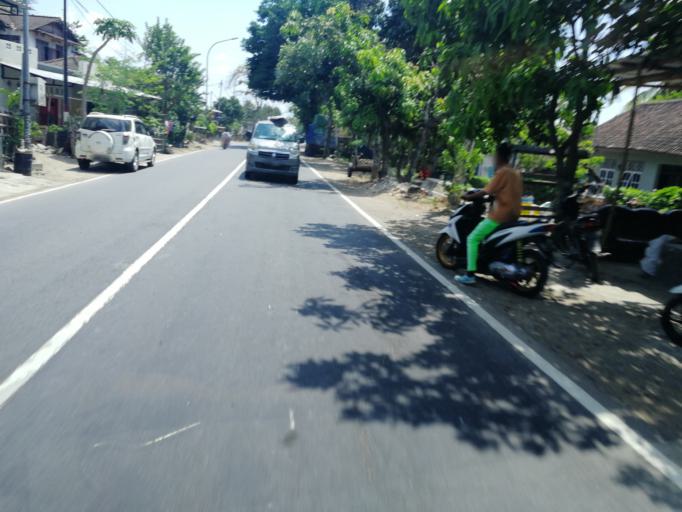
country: ID
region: West Nusa Tenggara
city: Jelateng Timur
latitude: -8.7069
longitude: 116.0849
